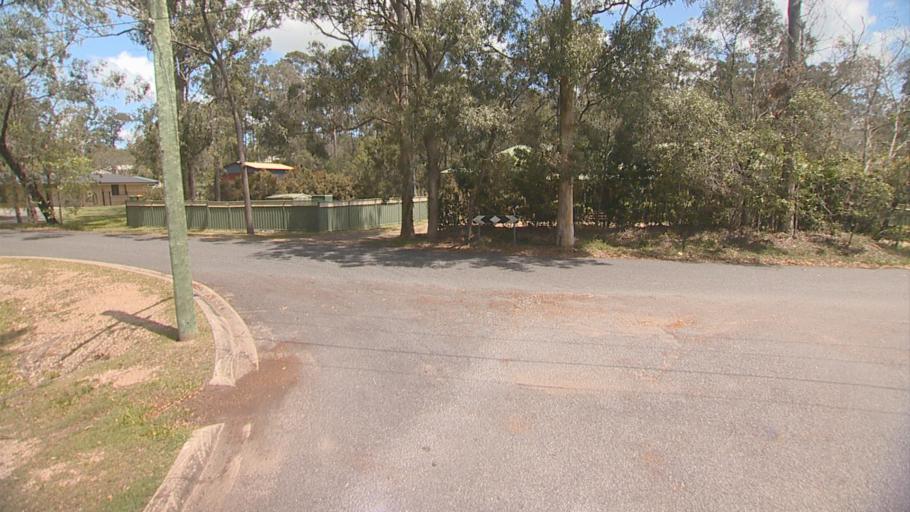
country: AU
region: Queensland
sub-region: Logan
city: Beenleigh
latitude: -27.6653
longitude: 153.2254
